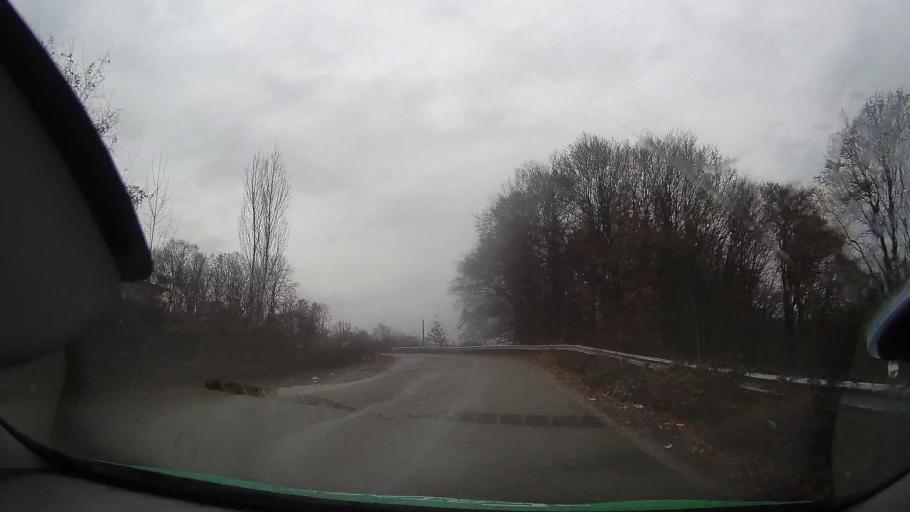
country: RO
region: Bihor
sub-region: Comuna Rabagani
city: Rabagani
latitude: 46.7272
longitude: 22.2400
